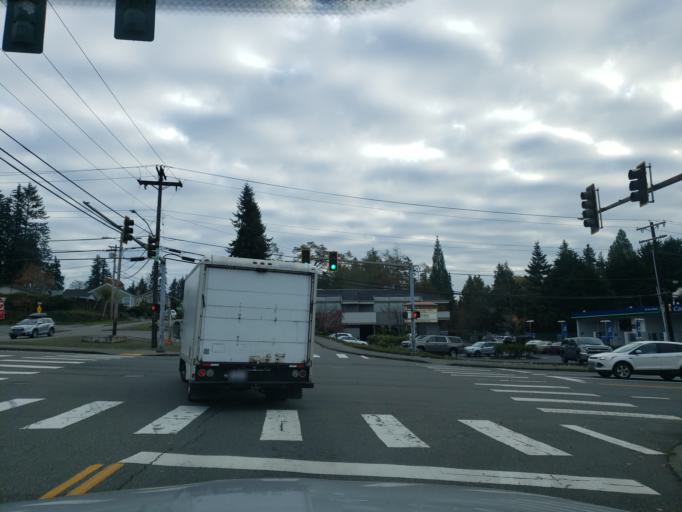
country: US
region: Washington
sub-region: Snohomish County
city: Everett
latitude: 47.9351
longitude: -122.2291
